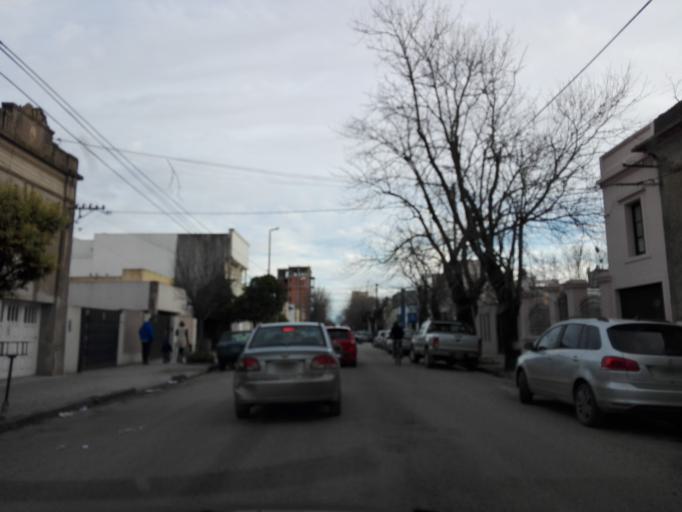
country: AR
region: Buenos Aires
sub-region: Partido de Balcarce
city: Balcarce
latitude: -37.8467
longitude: -58.2519
